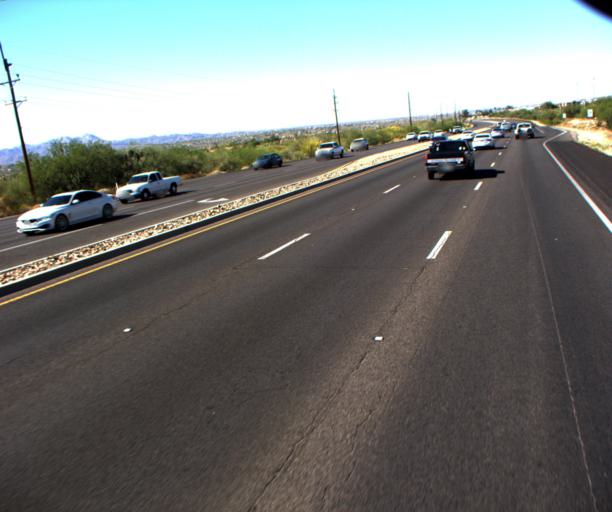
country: US
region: Arizona
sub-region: Pima County
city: Oro Valley
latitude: 32.3743
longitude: -110.9661
